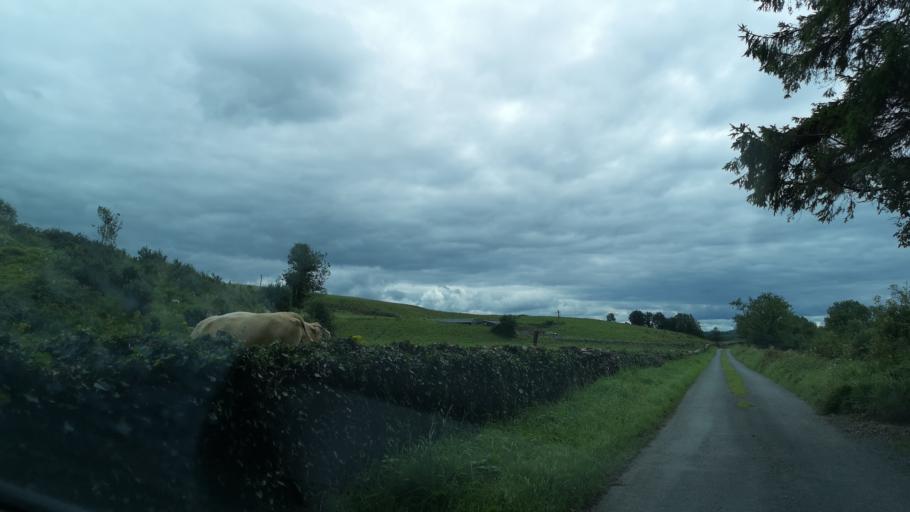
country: IE
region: Connaught
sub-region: County Galway
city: Loughrea
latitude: 53.1644
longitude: -8.4535
